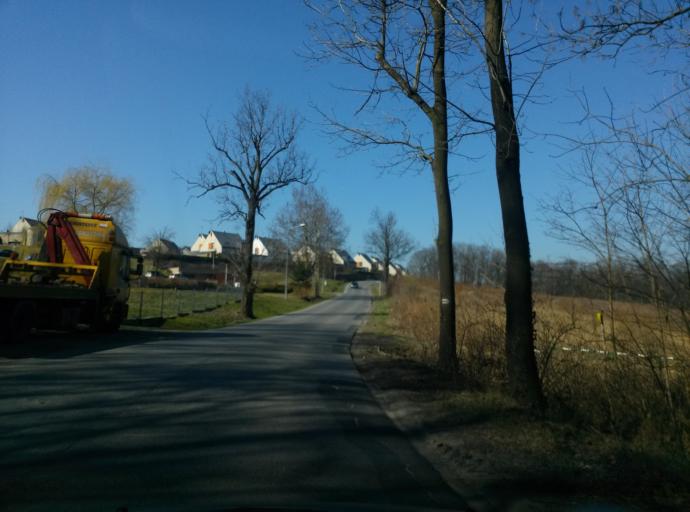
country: PL
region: Lesser Poland Voivodeship
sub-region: Powiat krakowski
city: Mogilany
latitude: 49.9447
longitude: 19.8794
